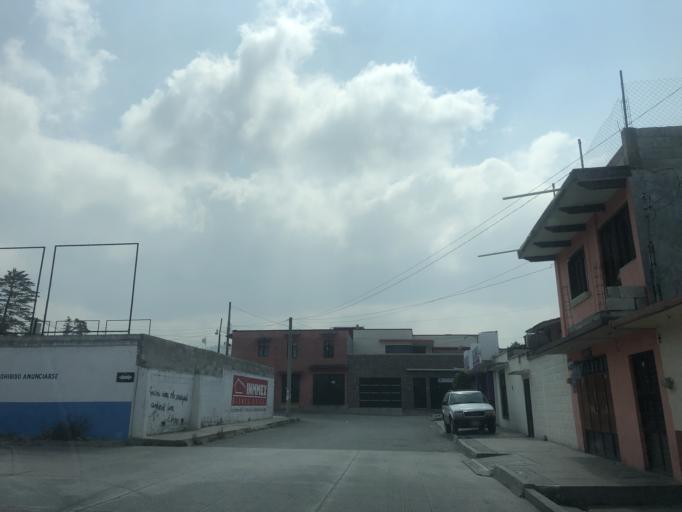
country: MX
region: Chiapas
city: San Cristobal de las Casas
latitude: 16.7207
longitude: -92.6413
